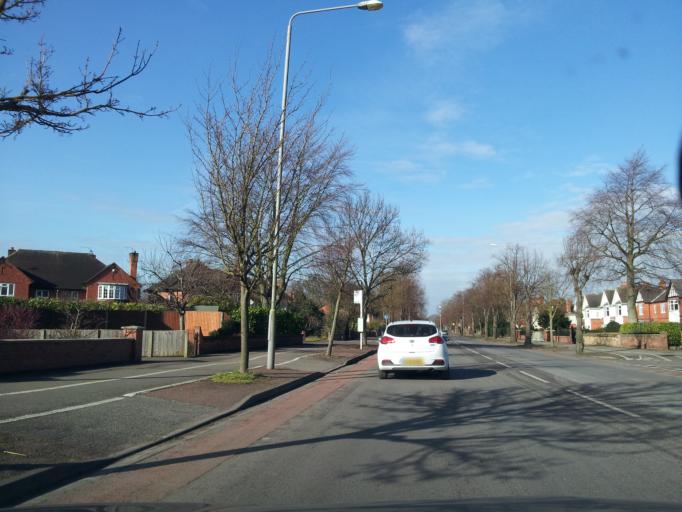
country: GB
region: England
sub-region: Nottinghamshire
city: Newark on Trent
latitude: 53.0675
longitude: -0.7955
